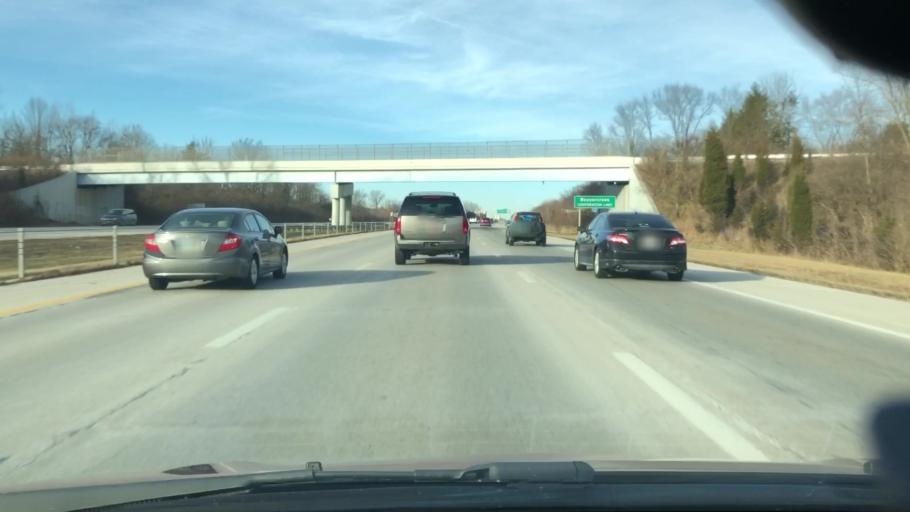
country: US
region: Ohio
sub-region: Greene County
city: Beavercreek
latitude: 39.6820
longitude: -84.1001
